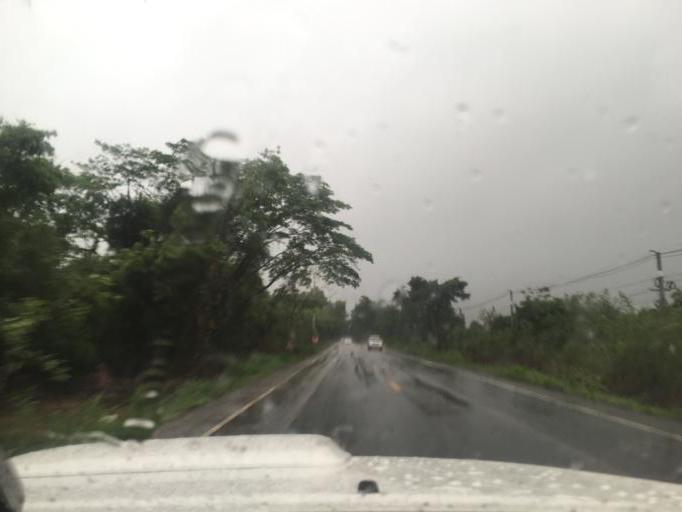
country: TH
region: Changwat Udon Thani
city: Udon Thani
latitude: 17.3419
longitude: 102.7172
